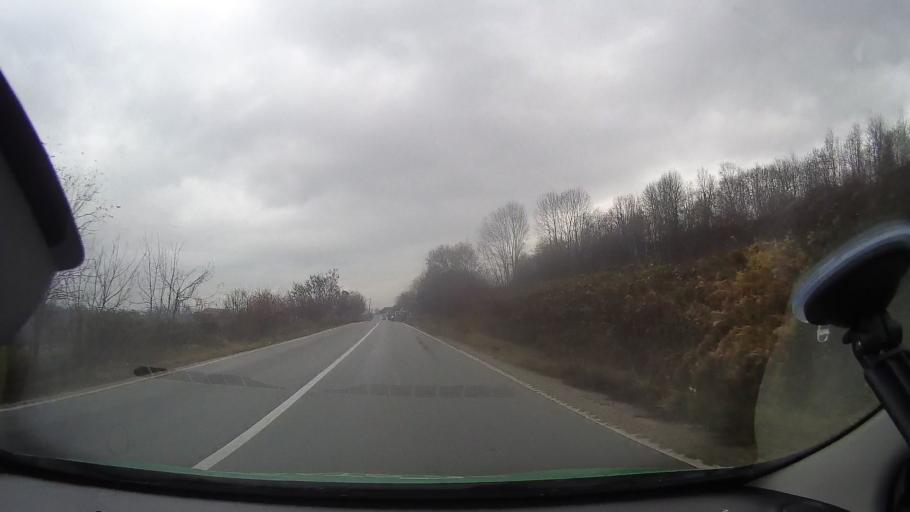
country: RO
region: Arad
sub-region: Comuna Almas
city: Almas
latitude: 46.2910
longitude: 22.2185
